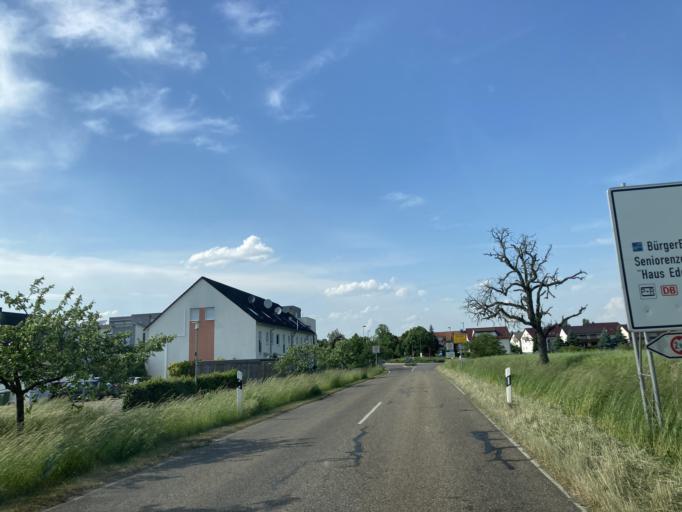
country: DE
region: Baden-Wuerttemberg
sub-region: Karlsruhe Region
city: Karlsdorf-Neuthard
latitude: 49.1000
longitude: 8.4842
